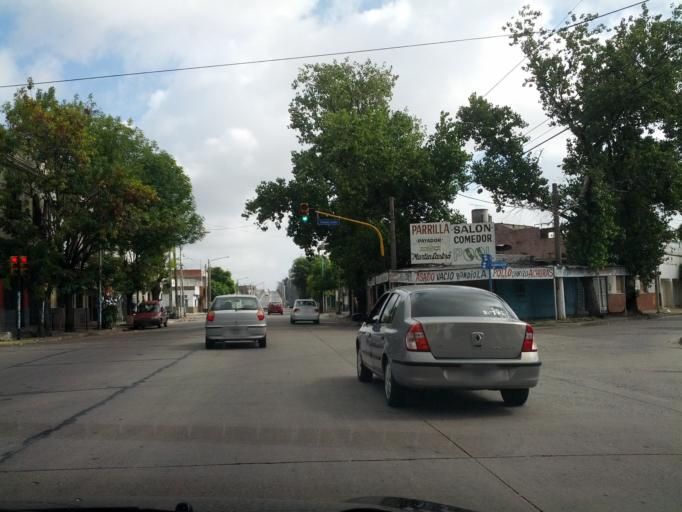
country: AR
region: Buenos Aires
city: San Justo
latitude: -34.6426
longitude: -58.5454
